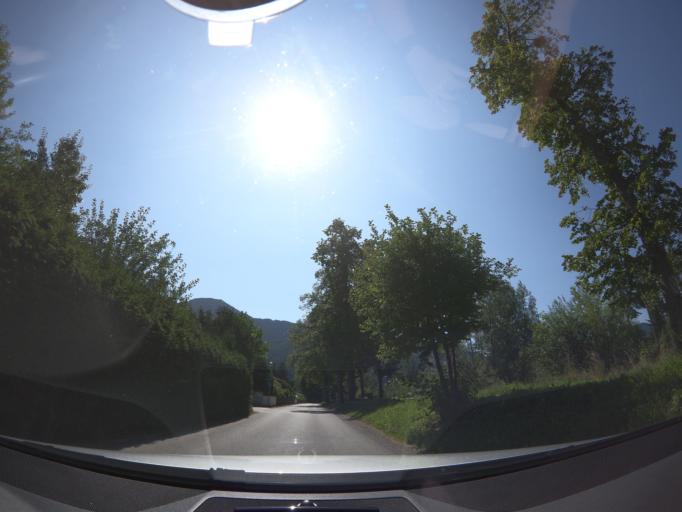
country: DE
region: Bavaria
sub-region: Upper Bavaria
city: Rottach-Egern
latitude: 47.6833
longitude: 11.7645
